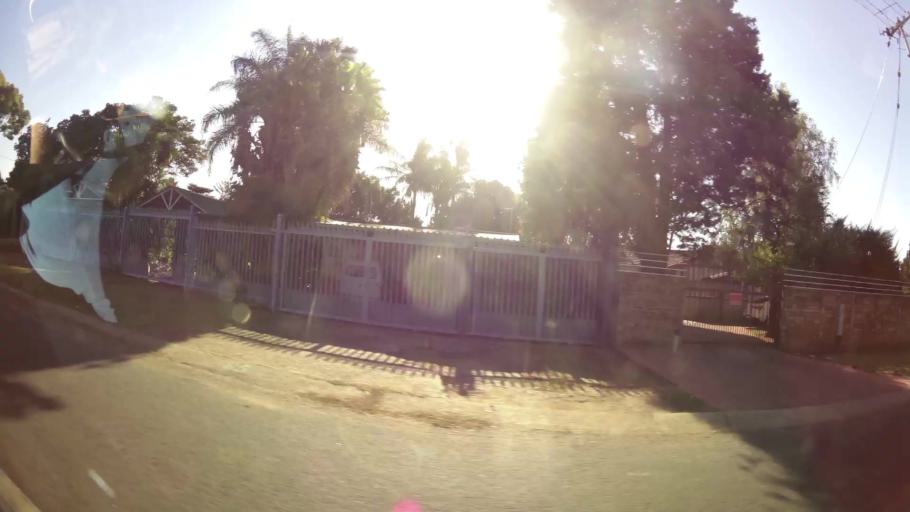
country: ZA
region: Gauteng
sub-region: City of Tshwane Metropolitan Municipality
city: Pretoria
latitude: -25.7140
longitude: 28.2633
